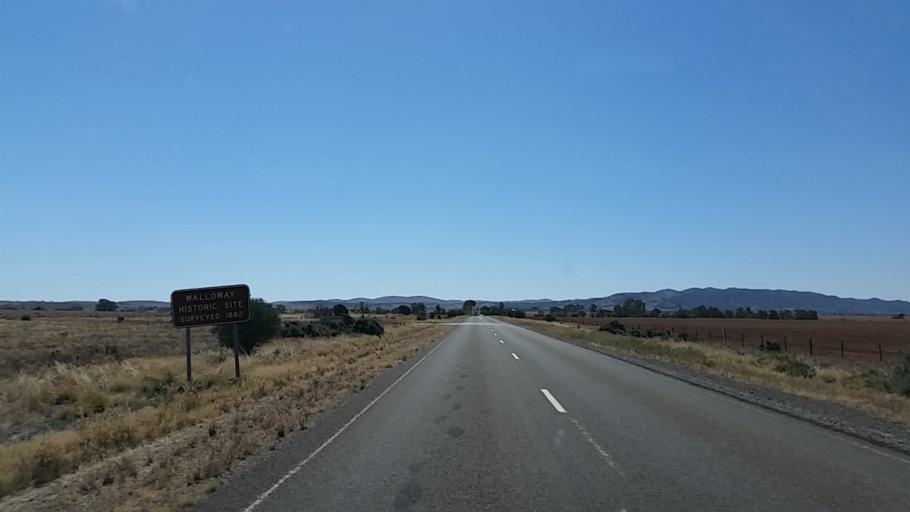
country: AU
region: South Australia
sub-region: Peterborough
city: Peterborough
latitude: -32.6447
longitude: 138.5999
